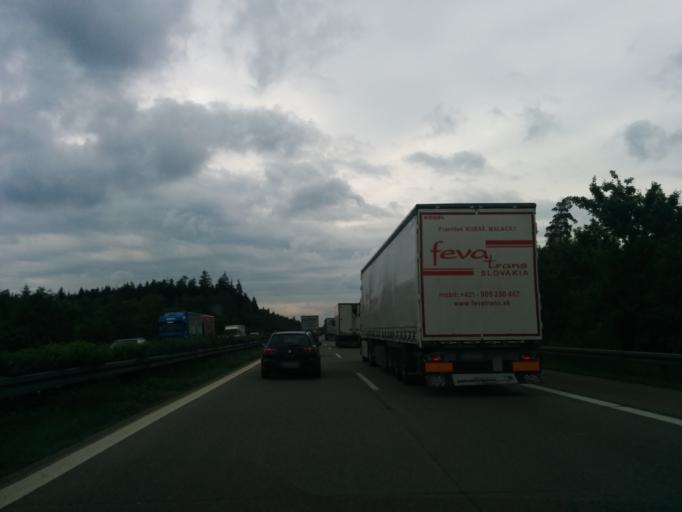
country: DE
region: Baden-Wuerttemberg
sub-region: Regierungsbezirk Stuttgart
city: Ellenberg
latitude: 49.0346
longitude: 10.1888
